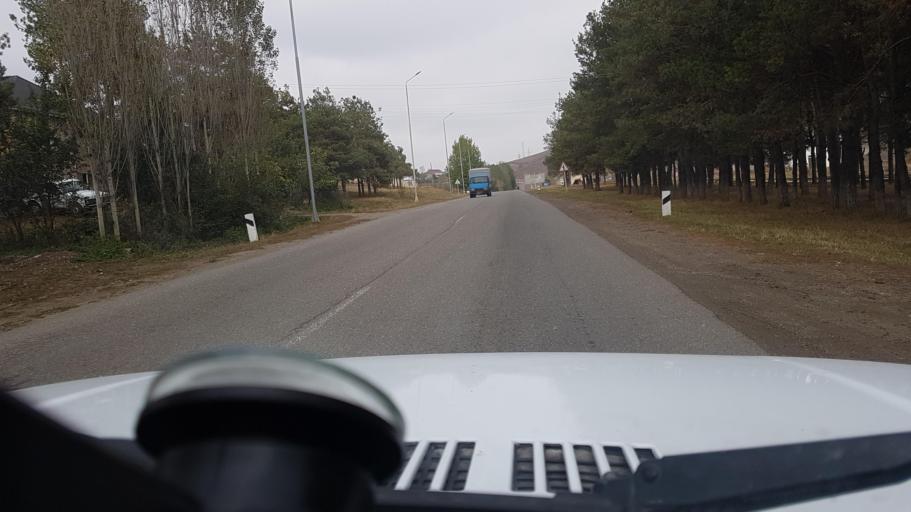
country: AZ
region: Gadabay Rayon
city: Ariqdam
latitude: 40.6049
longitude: 45.8123
